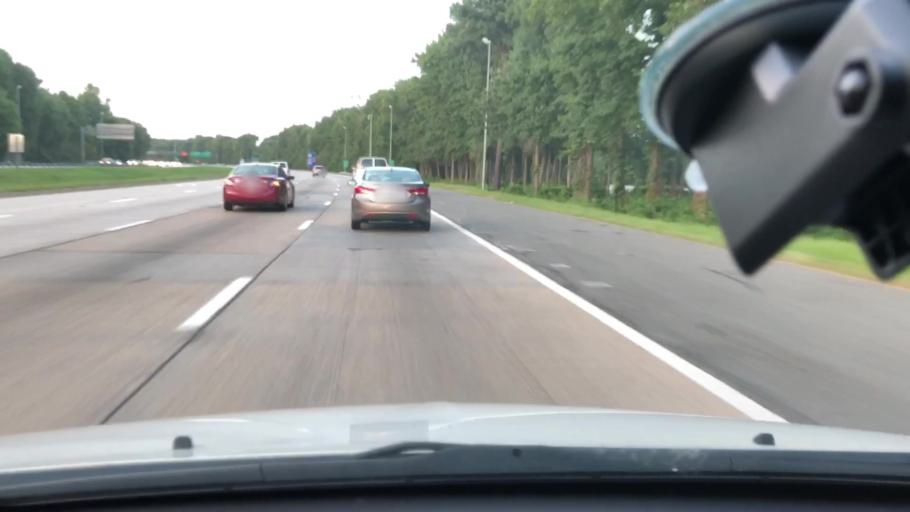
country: US
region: Virginia
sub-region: City of Chesapeake
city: Chesapeake
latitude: 36.7994
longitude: -76.2019
